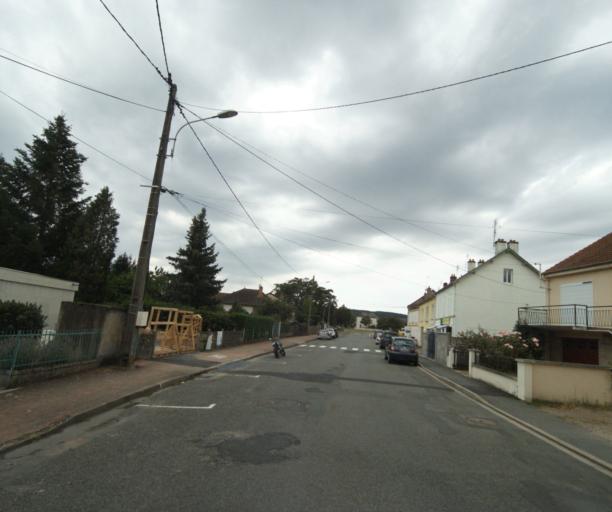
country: FR
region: Bourgogne
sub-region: Departement de Saone-et-Loire
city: Gueugnon
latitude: 46.6006
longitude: 4.0577
